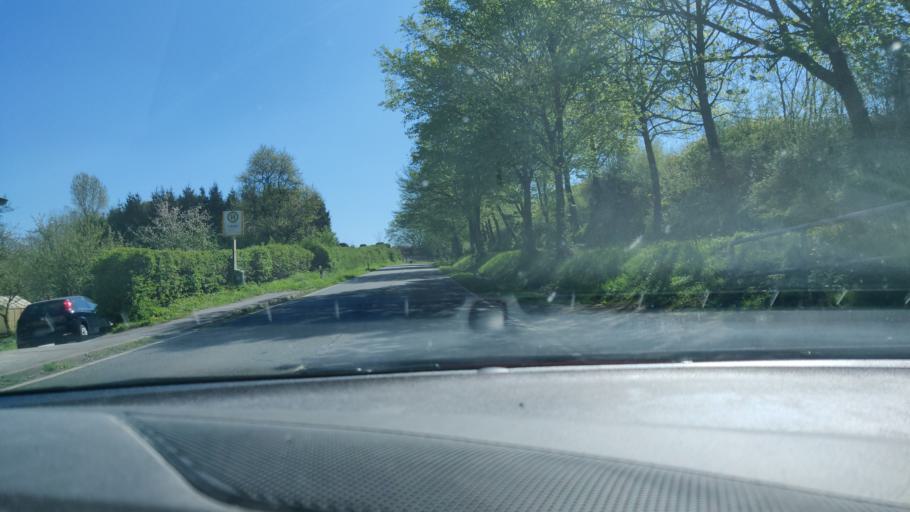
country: DE
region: North Rhine-Westphalia
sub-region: Regierungsbezirk Dusseldorf
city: Mettmann
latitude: 51.2370
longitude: 6.9903
